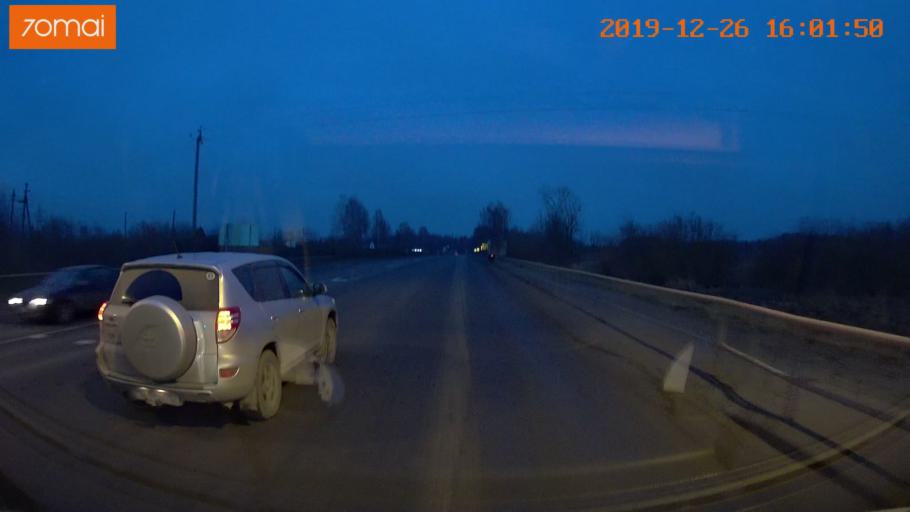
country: RU
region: Jaroslavl
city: Rybinsk
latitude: 58.0153
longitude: 38.8231
